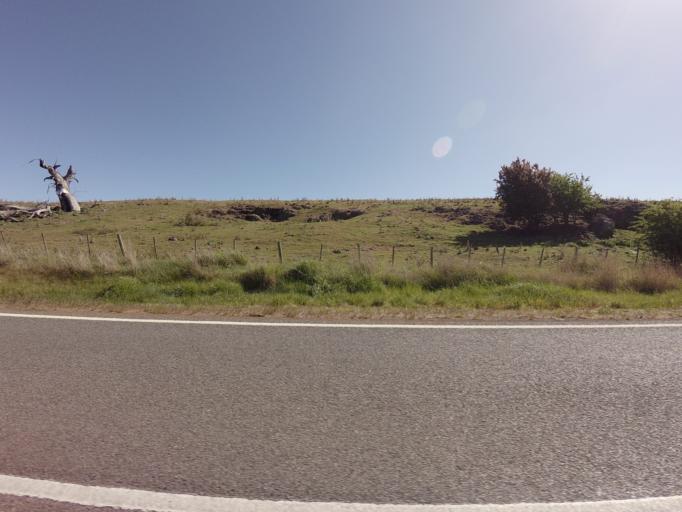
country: AU
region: Tasmania
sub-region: Derwent Valley
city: New Norfolk
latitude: -42.6419
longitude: 146.9193
